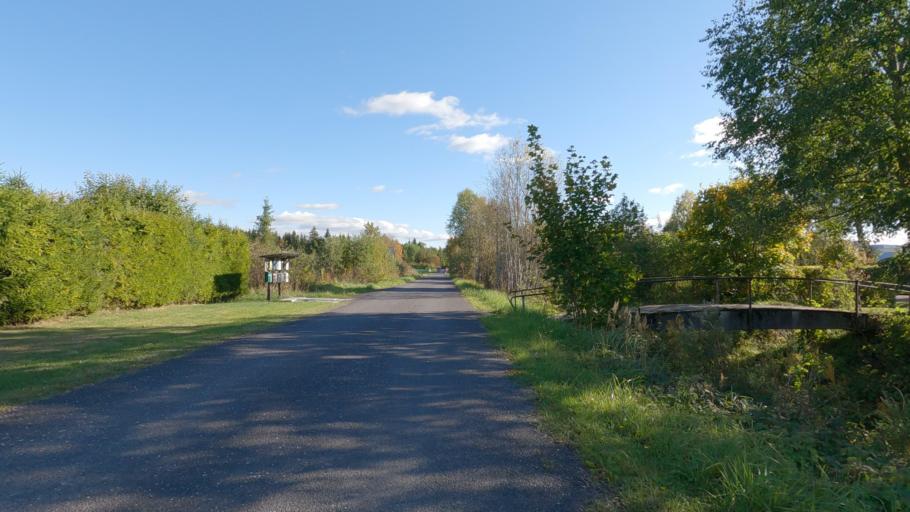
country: EE
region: Raplamaa
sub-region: Rapla vald
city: Rapla
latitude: 58.9940
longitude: 24.8341
